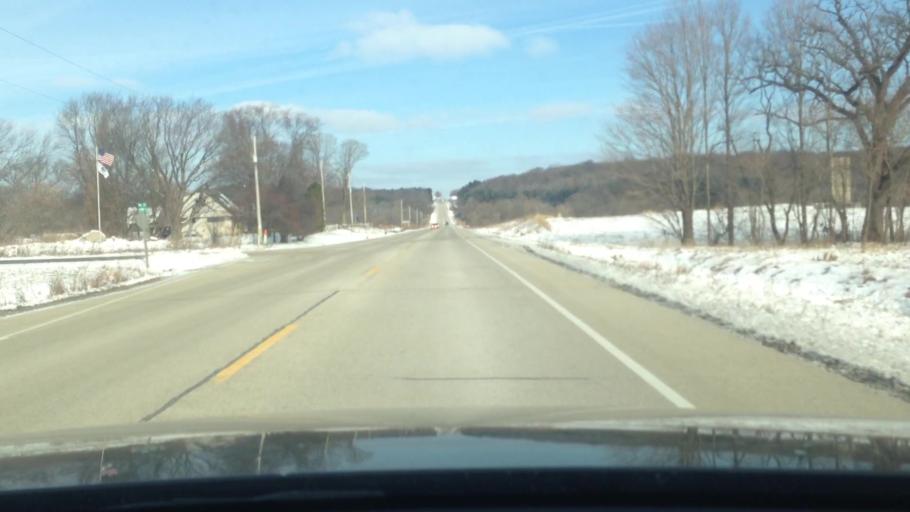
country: US
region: Wisconsin
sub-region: Walworth County
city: East Troy
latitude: 42.7269
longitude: -88.4056
